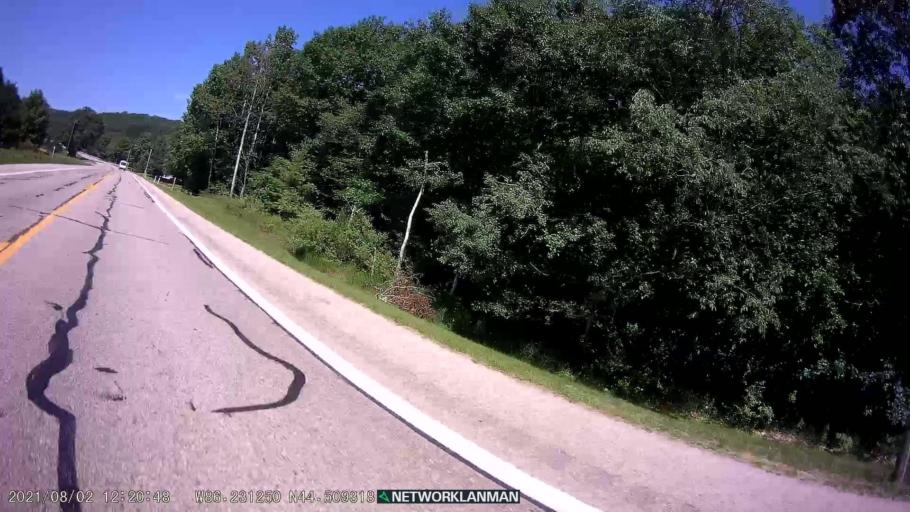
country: US
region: Michigan
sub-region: Benzie County
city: Frankfort
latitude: 44.5097
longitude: -86.2312
